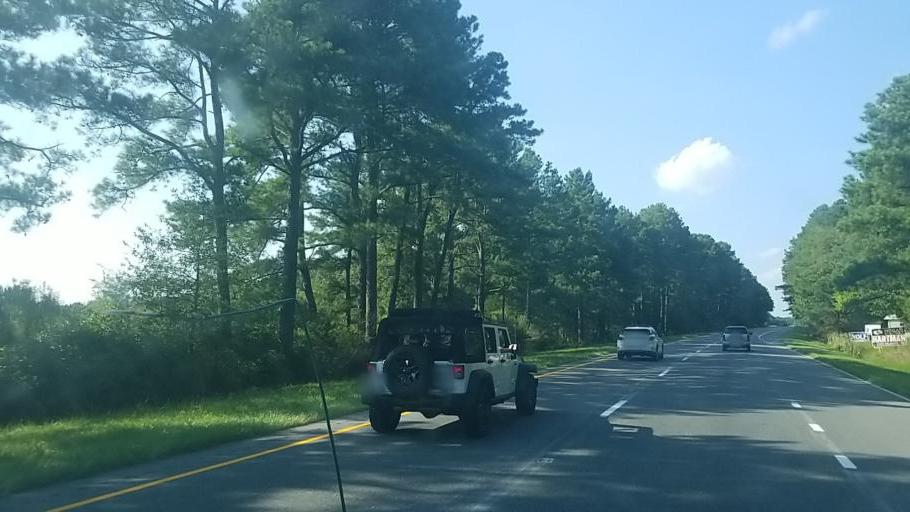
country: US
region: Maryland
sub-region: Worcester County
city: Berlin
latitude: 38.3491
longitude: -75.2146
